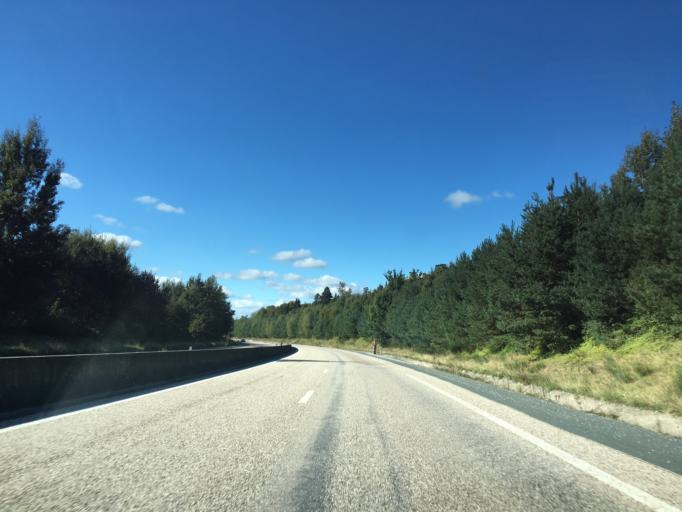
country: FR
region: Lorraine
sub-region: Departement de Meurthe-et-Moselle
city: Baccarat
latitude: 48.4359
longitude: 6.7793
